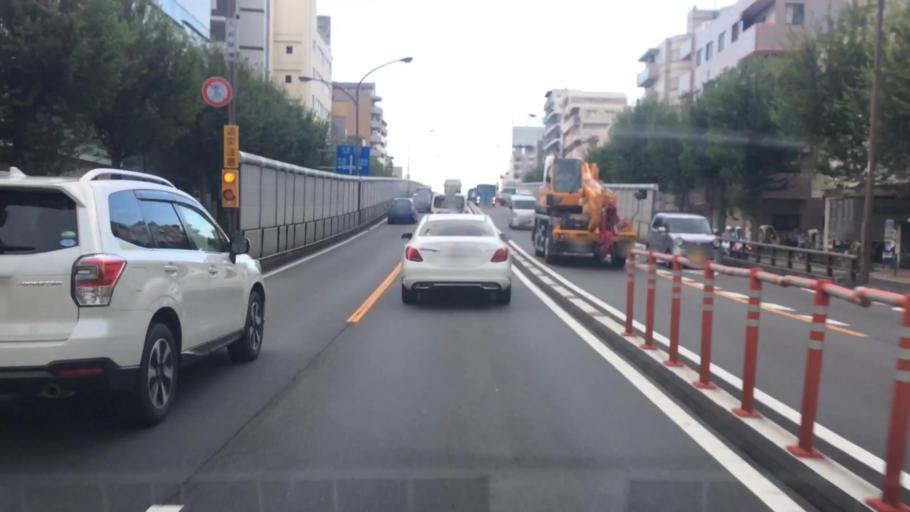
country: JP
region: Tokyo
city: Tokyo
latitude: 35.7114
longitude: 139.6540
